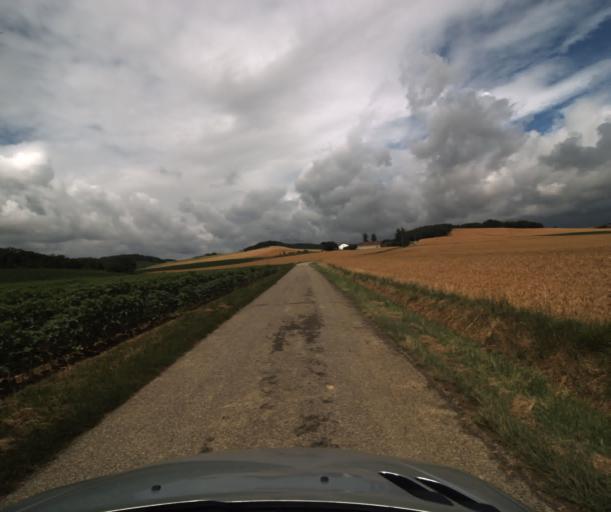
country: FR
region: Midi-Pyrenees
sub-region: Departement du Tarn-et-Garonne
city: Lavit
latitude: 43.9547
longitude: 0.9050
